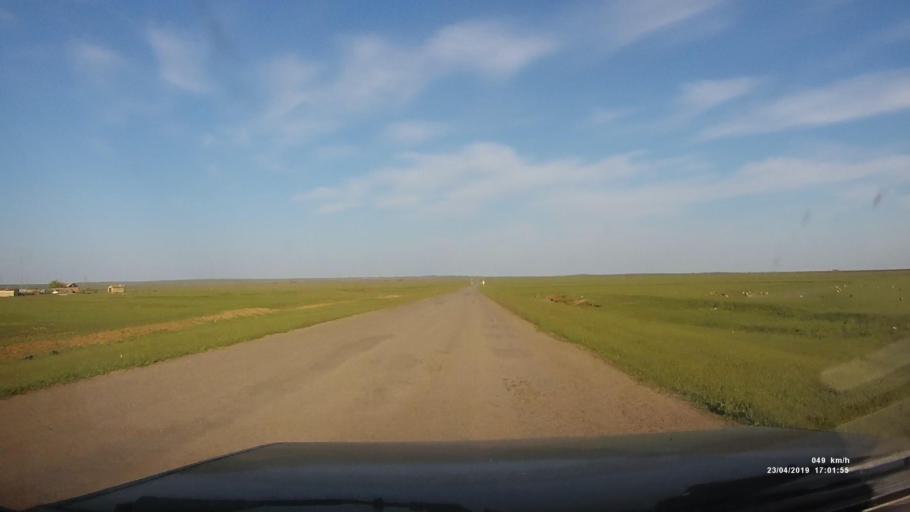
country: RU
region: Kalmykiya
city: Priyutnoye
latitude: 46.2942
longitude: 43.4114
